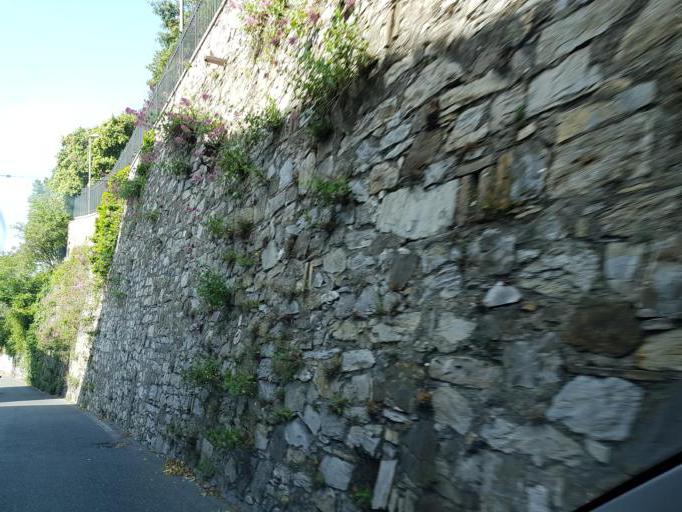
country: IT
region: Liguria
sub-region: Provincia di Genova
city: Genoa
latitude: 44.4240
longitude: 8.9252
